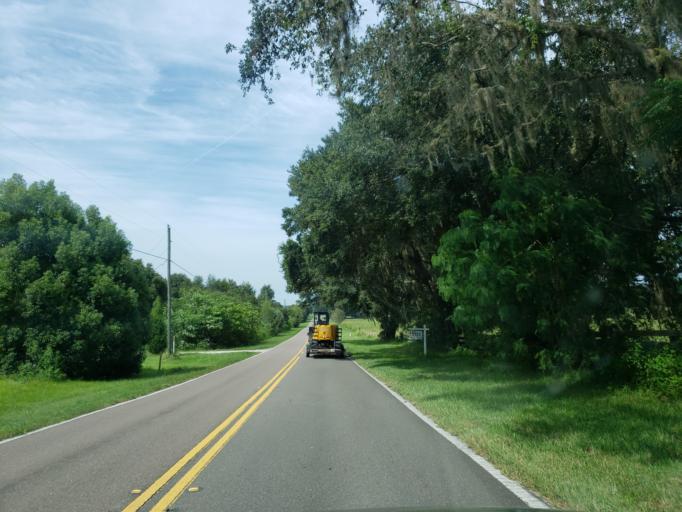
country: US
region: Florida
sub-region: Pasco County
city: San Antonio
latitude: 28.3068
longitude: -82.2786
